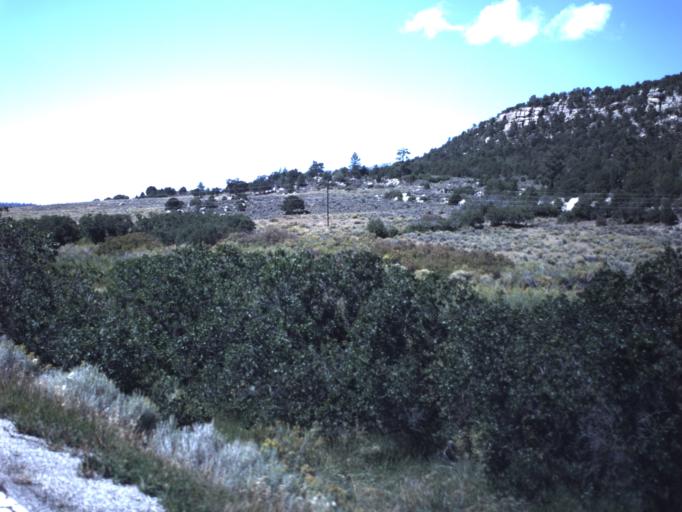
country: US
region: Utah
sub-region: Grand County
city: Moab
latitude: 38.3288
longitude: -109.1175
